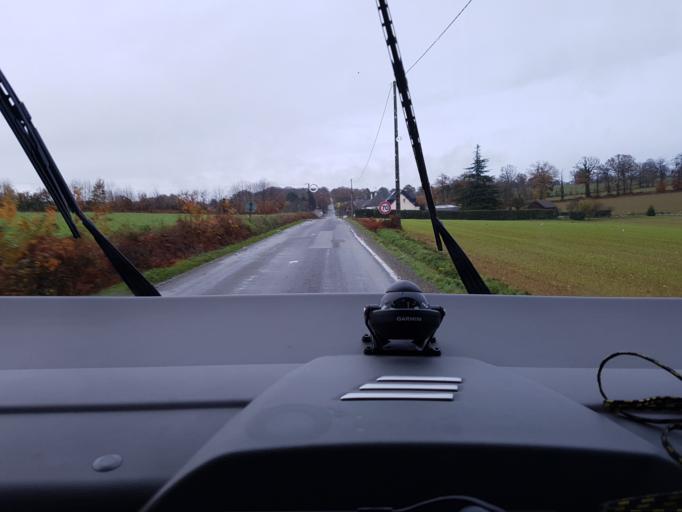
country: FR
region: Brittany
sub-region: Departement d'Ille-et-Vilaine
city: Vitre
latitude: 48.1304
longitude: -1.1658
